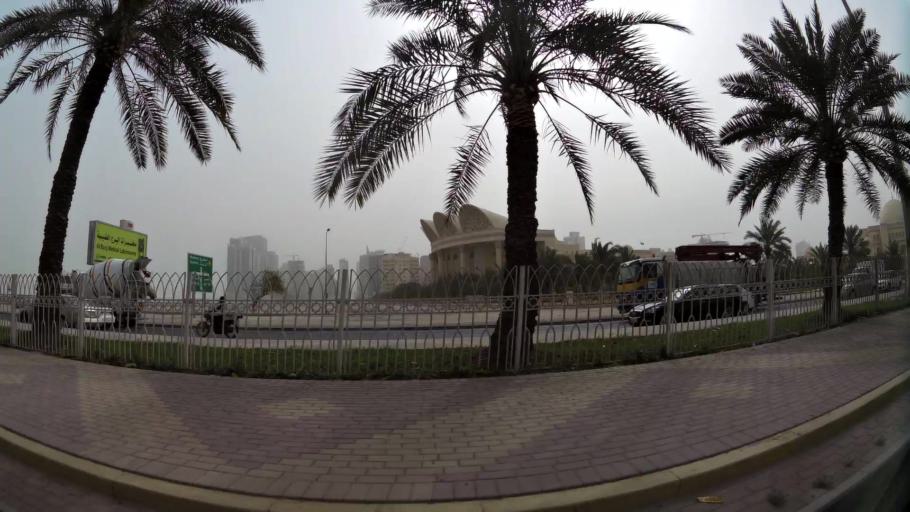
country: BH
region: Manama
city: Manama
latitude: 26.2213
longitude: 50.5974
